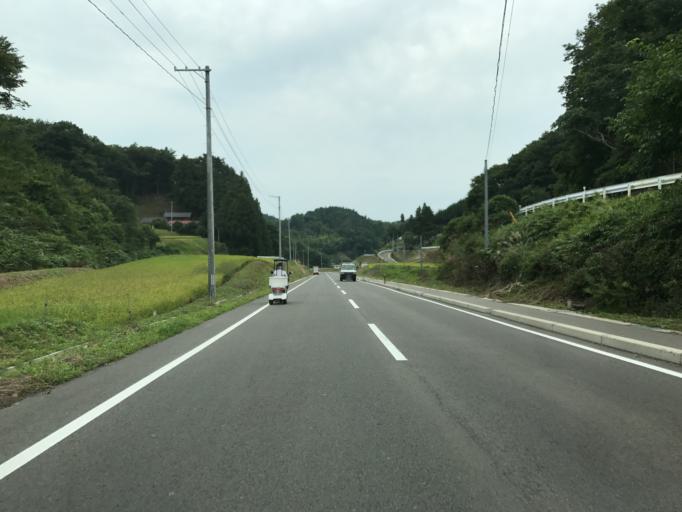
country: JP
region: Fukushima
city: Funehikimachi-funehiki
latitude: 37.6246
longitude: 140.6435
